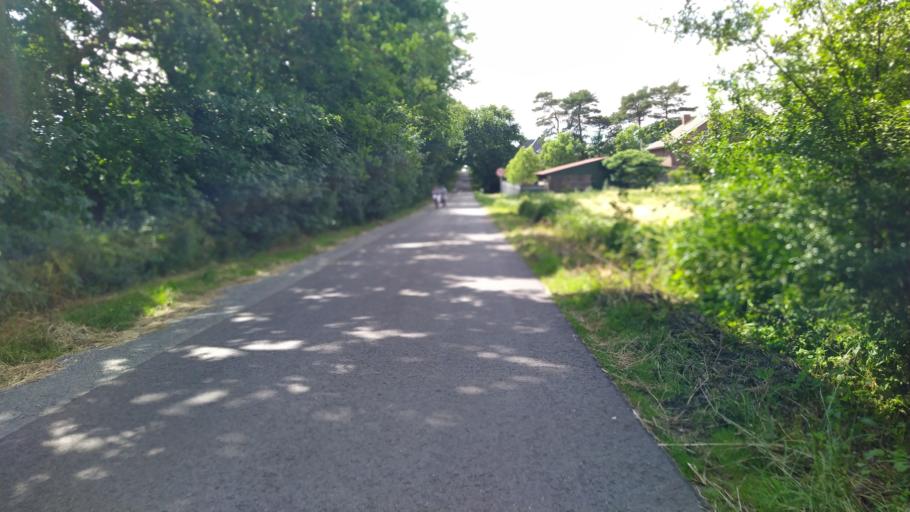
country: DE
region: Lower Saxony
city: Hollnseth
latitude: 53.5960
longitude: 9.0948
